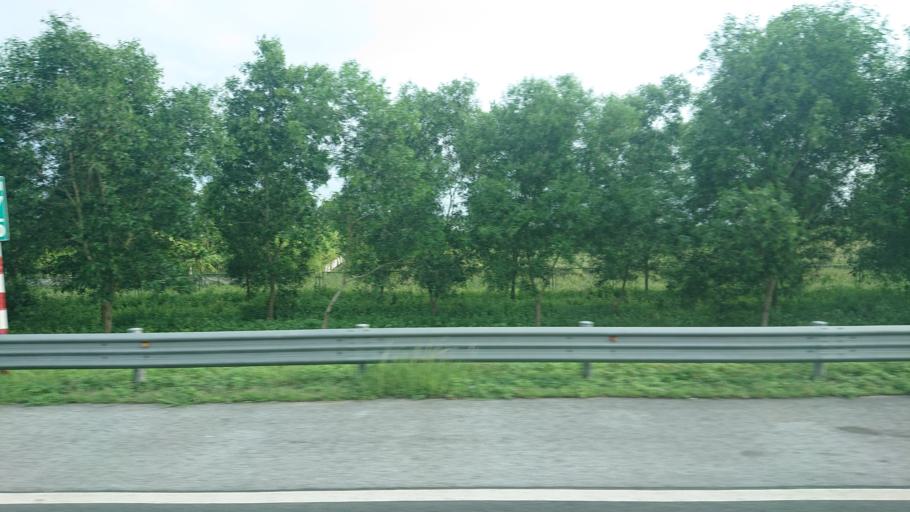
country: VN
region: Hai Phong
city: An Lao
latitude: 20.8009
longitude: 106.5318
